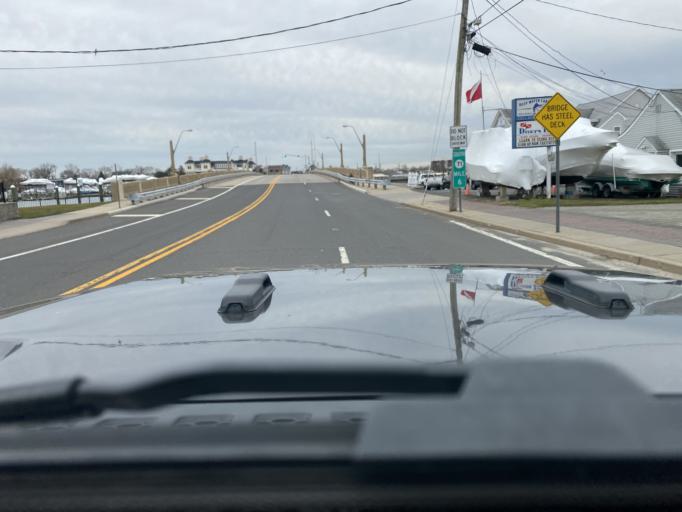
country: US
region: New Jersey
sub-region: Monmouth County
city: Avon-by-the-Sea
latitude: 40.1877
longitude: -74.0233
